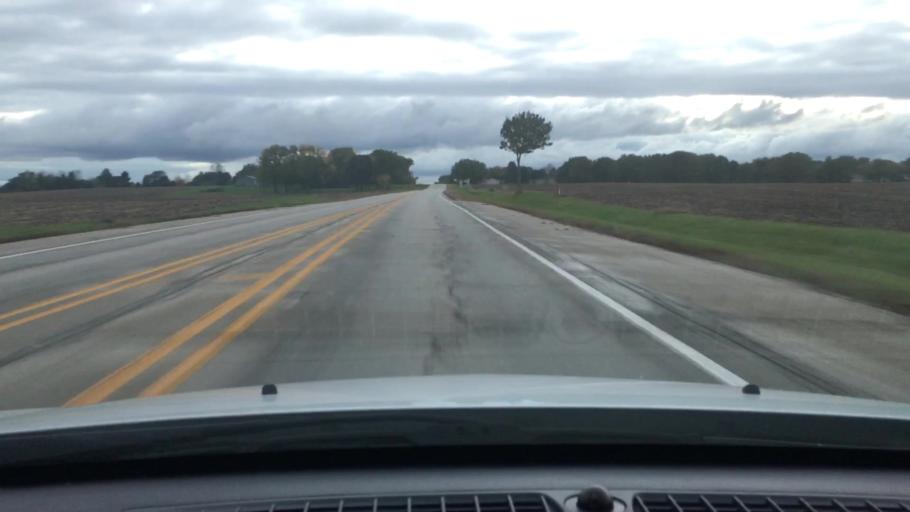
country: US
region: Illinois
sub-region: DeKalb County
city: Malta
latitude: 41.9362
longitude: -88.8147
